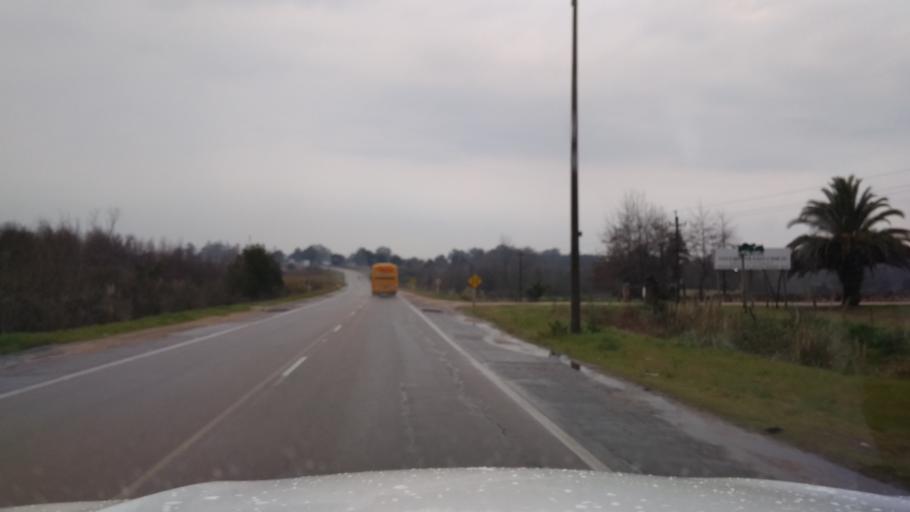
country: UY
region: Canelones
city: Toledo
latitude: -34.7518
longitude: -56.1062
